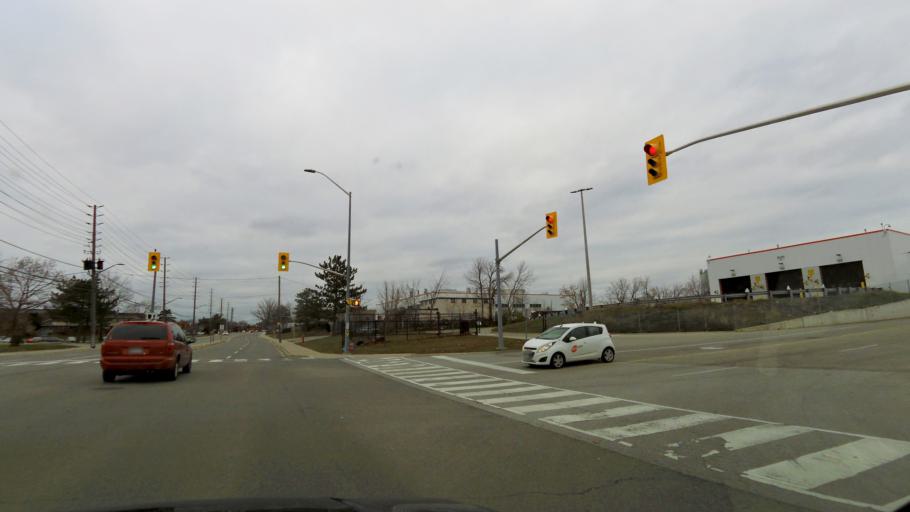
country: CA
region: Ontario
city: Mississauga
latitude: 43.5681
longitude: -79.6576
